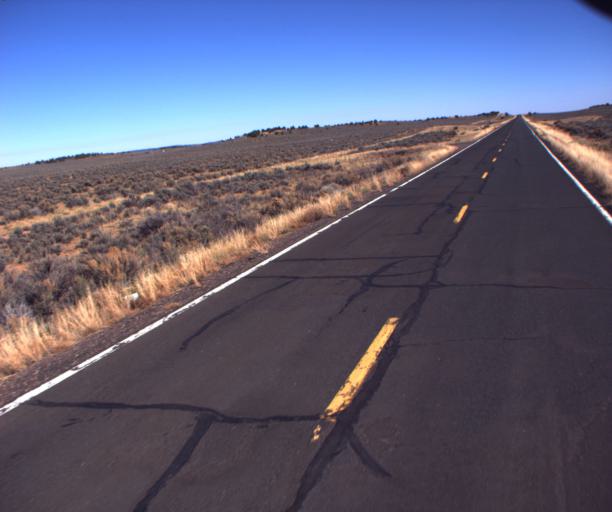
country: US
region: Arizona
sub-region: Navajo County
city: First Mesa
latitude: 35.7469
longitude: -110.0536
